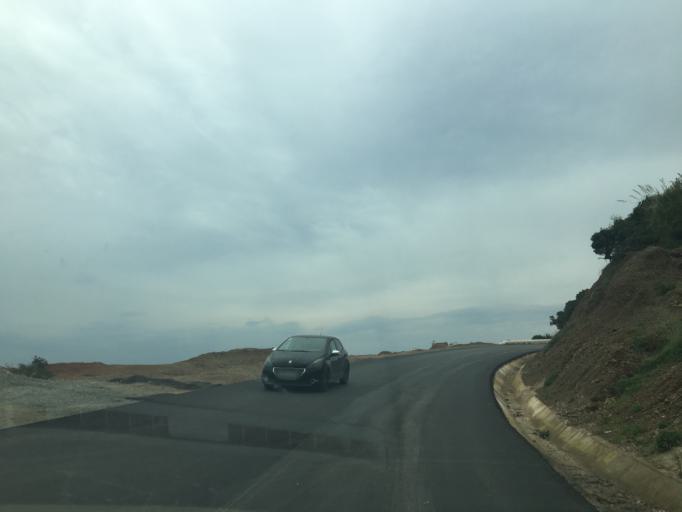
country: DZ
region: Tipaza
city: Tipasa
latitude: 36.6402
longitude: 2.3395
